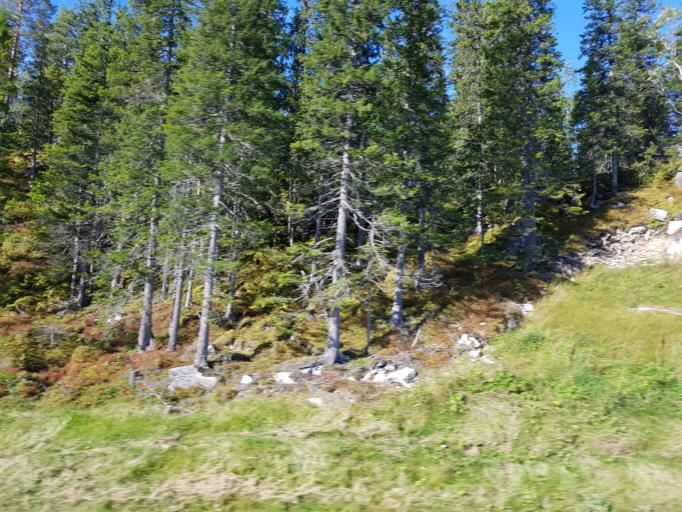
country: NO
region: Sor-Trondelag
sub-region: Trondheim
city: Trondheim
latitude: 63.6112
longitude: 10.2377
